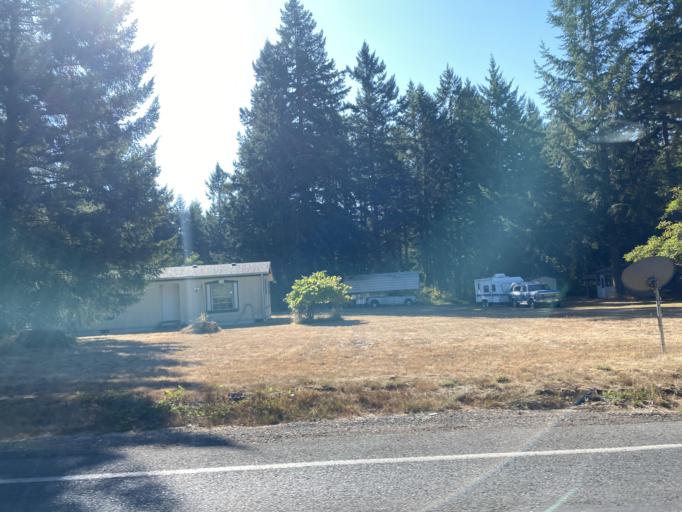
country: US
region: Washington
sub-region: Thurston County
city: Rainier
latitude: 46.9014
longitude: -122.7221
